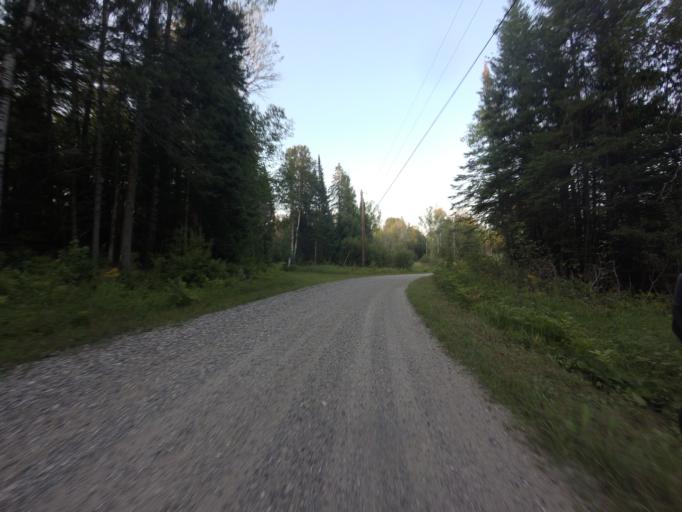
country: CA
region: Ontario
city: Renfrew
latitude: 45.0728
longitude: -76.7497
